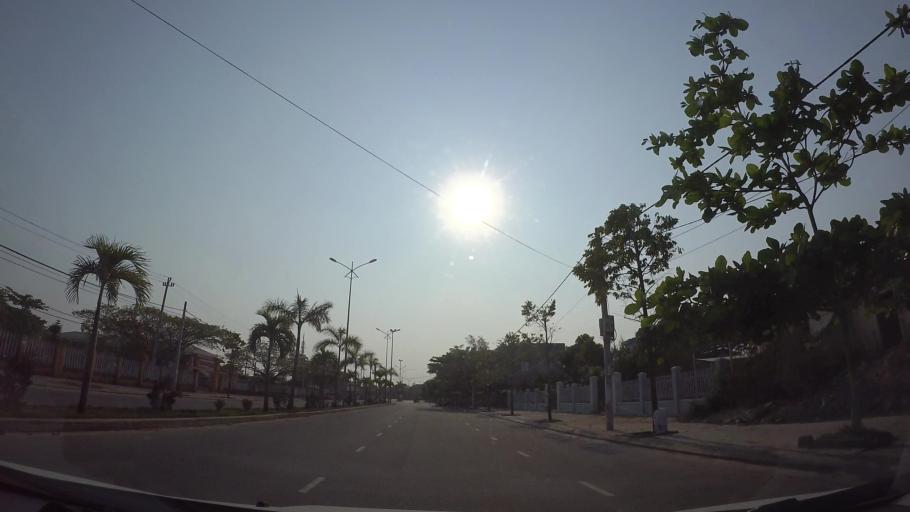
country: VN
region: Da Nang
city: Ngu Hanh Son
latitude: 15.9570
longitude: 108.2576
